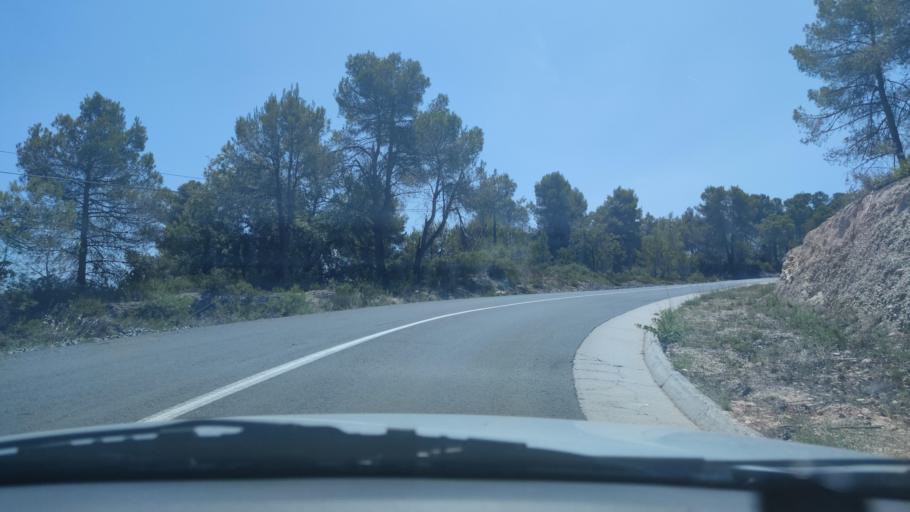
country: ES
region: Catalonia
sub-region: Provincia de Lleida
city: Vinaixa
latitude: 41.4080
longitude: 0.9582
